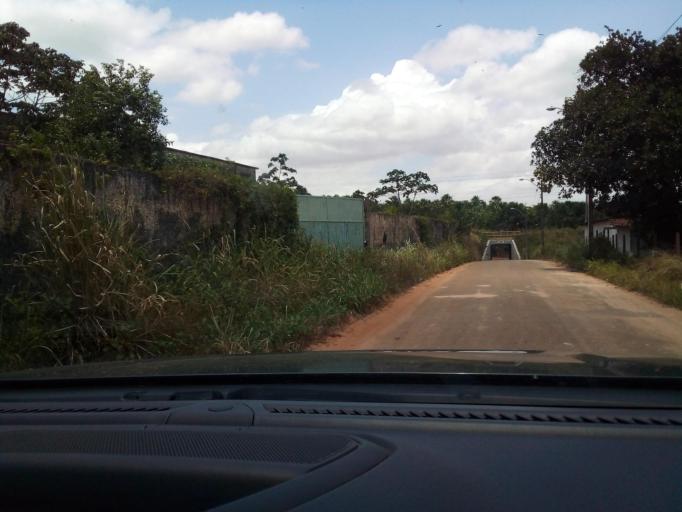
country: BR
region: Maranhao
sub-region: Sao Luis
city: Sao Luis
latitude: -2.7025
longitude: -44.3107
